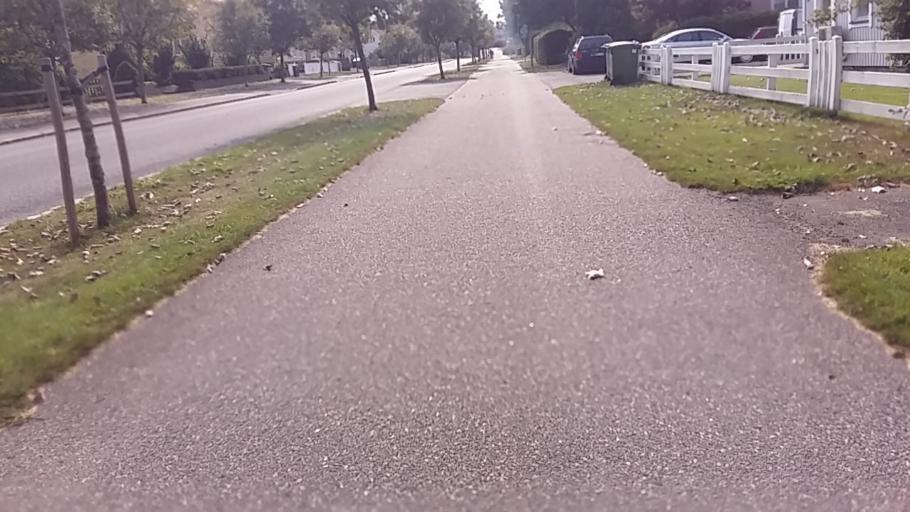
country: SE
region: Joenkoeping
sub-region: Jonkopings Kommun
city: Jonkoping
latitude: 57.7611
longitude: 14.1524
